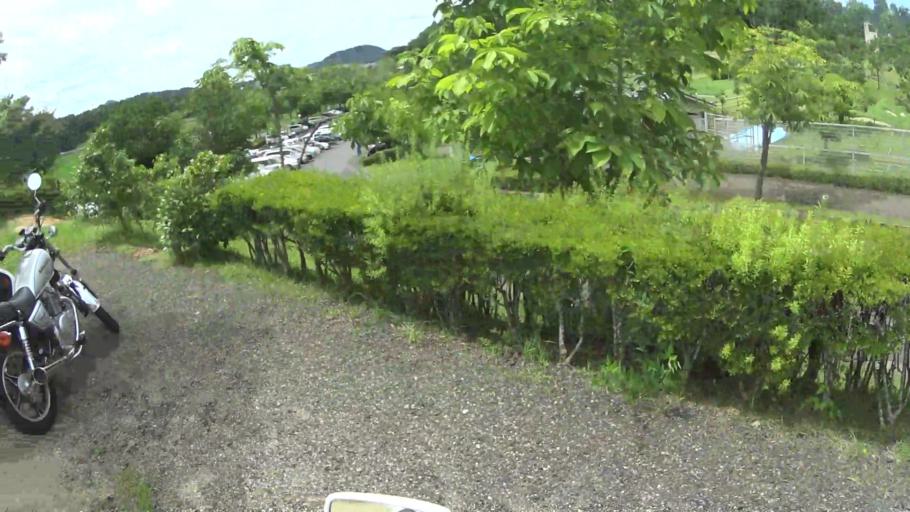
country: JP
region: Kyoto
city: Ayabe
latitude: 35.1624
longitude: 135.4153
